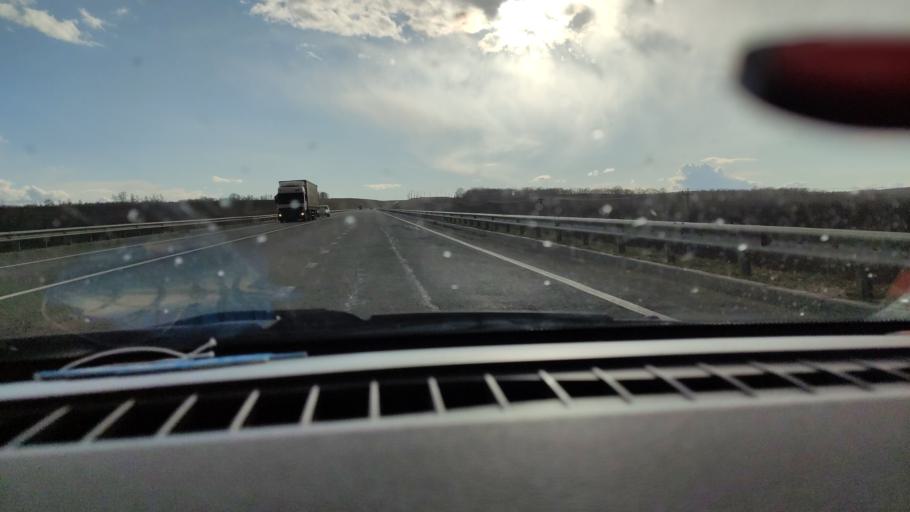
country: RU
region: Saratov
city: Yelshanka
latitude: 51.8212
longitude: 46.3713
